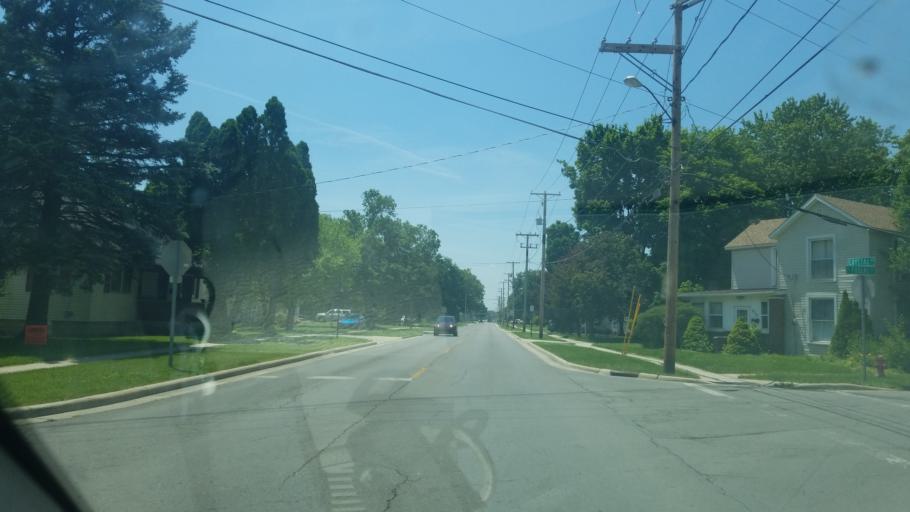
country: US
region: Ohio
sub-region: Hancock County
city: Findlay
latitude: 41.0579
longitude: -83.6381
